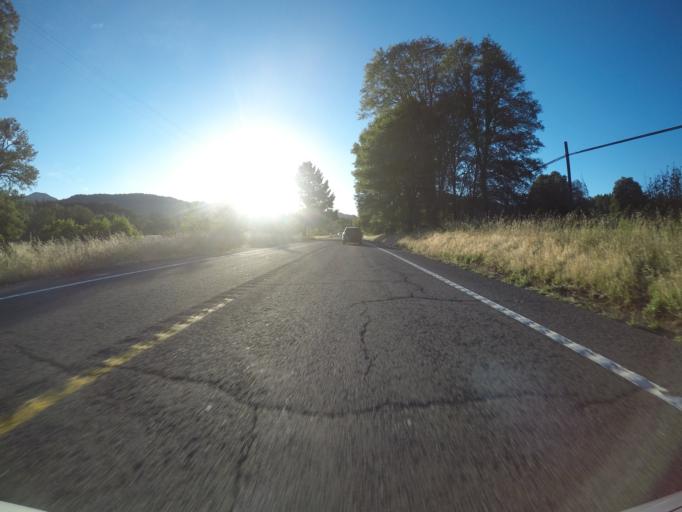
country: US
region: California
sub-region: Mendocino County
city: Laytonville
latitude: 39.7440
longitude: -123.5210
